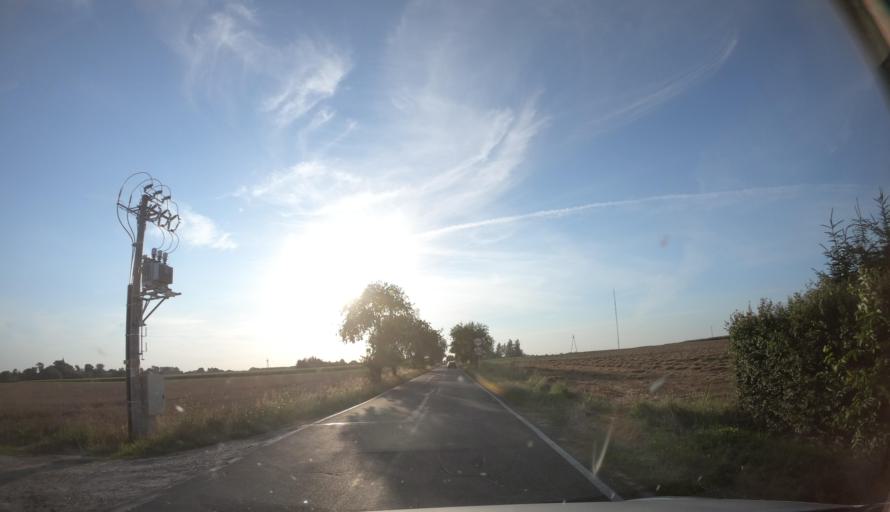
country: PL
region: Kujawsko-Pomorskie
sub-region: Powiat swiecki
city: Pruszcz
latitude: 53.2527
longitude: 18.1902
